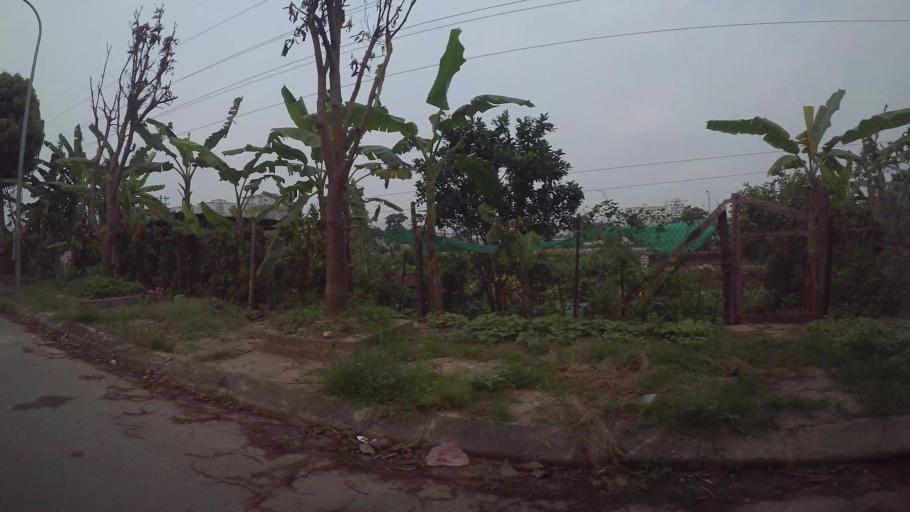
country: VN
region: Ha Noi
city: Trau Quy
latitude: 21.0536
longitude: 105.9056
